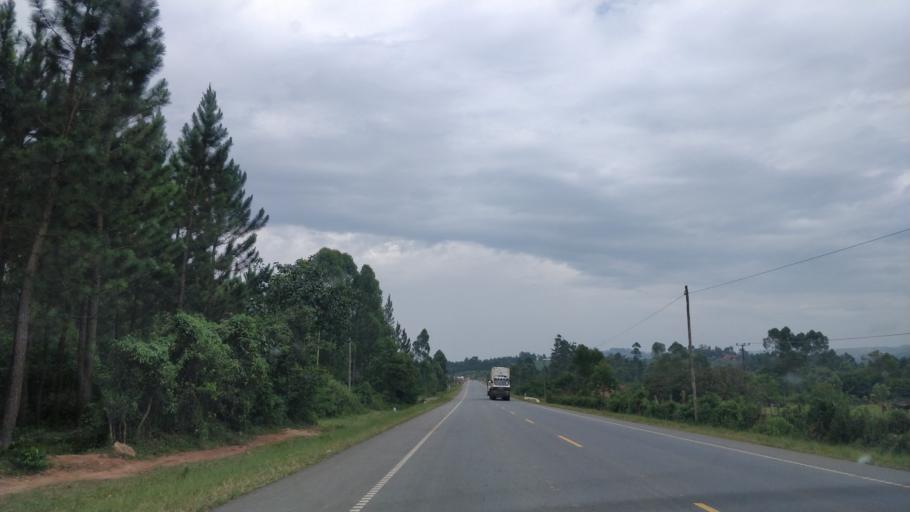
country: UG
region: Western Region
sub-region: Sheema District
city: Kibingo
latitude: -0.6696
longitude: 30.4384
